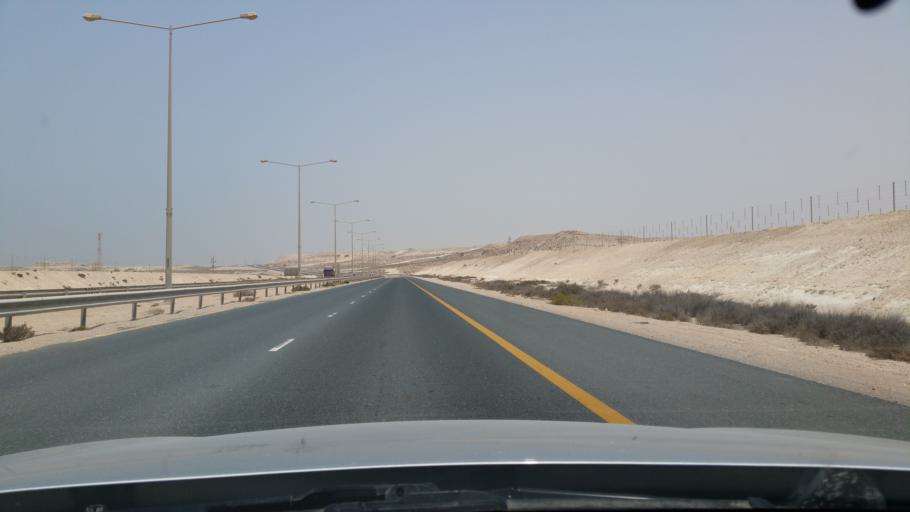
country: QA
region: Baladiyat ar Rayyan
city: Dukhan
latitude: 25.3413
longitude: 50.7833
